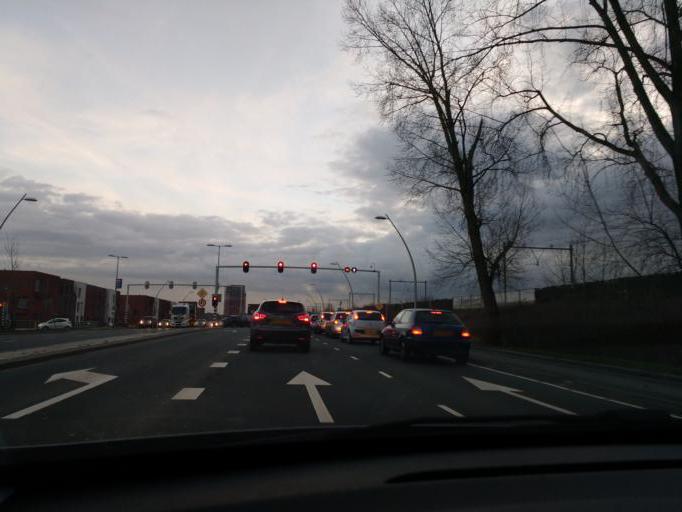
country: NL
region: Gelderland
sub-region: Gemeente Nijmegen
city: Nijmegen
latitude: 51.8698
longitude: 5.8596
